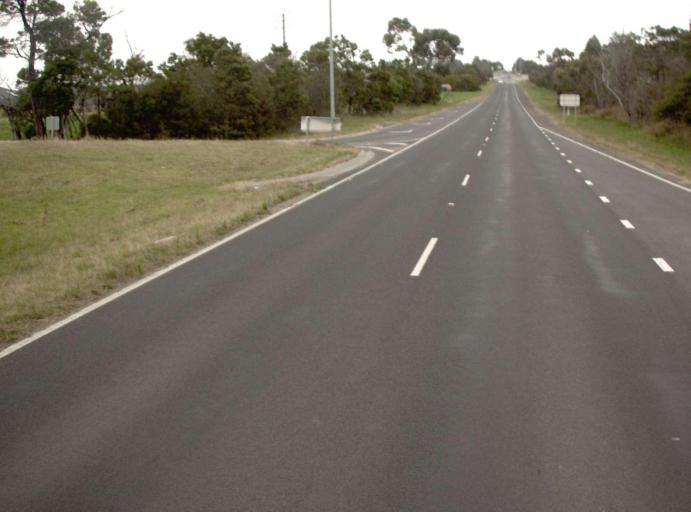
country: AU
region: Victoria
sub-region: Cardinia
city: Officer
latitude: -38.0613
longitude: 145.4428
